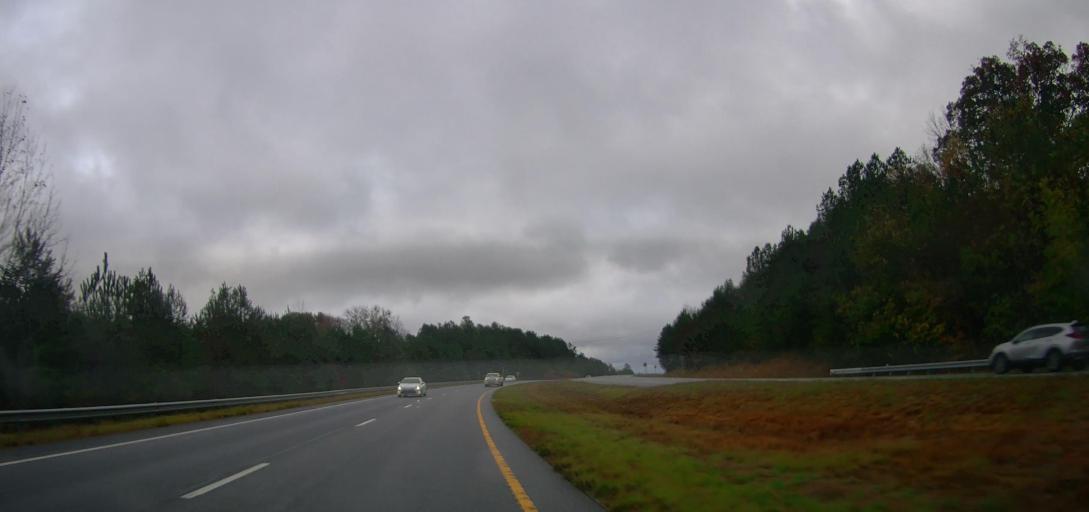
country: US
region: Georgia
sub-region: Habersham County
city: Baldwin
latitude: 34.4771
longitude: -83.5183
